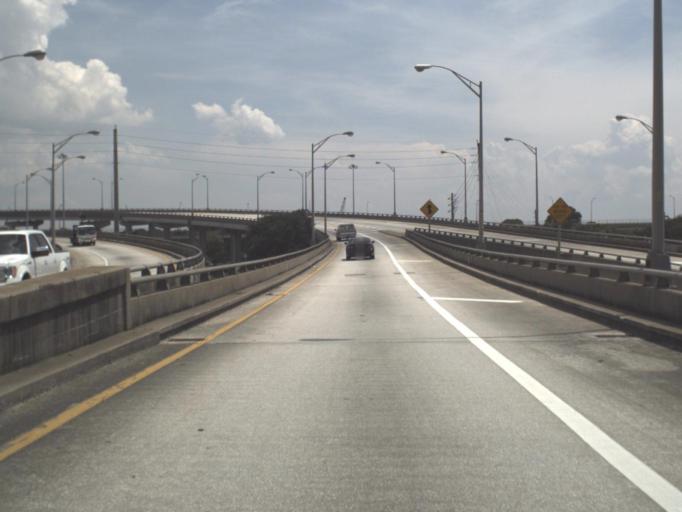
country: US
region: Florida
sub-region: Duval County
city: Jacksonville
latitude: 30.3235
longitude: -81.6346
